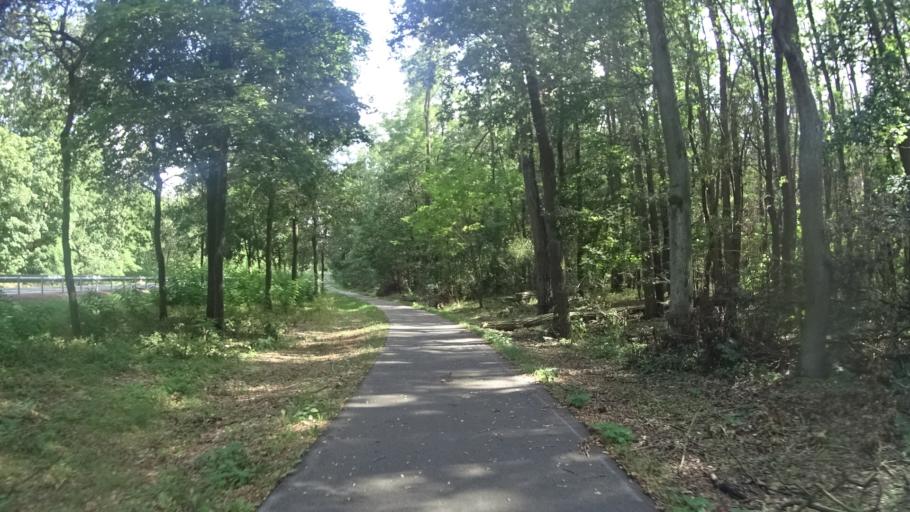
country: DE
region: Brandenburg
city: Rhinow
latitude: 52.7180
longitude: 12.3649
